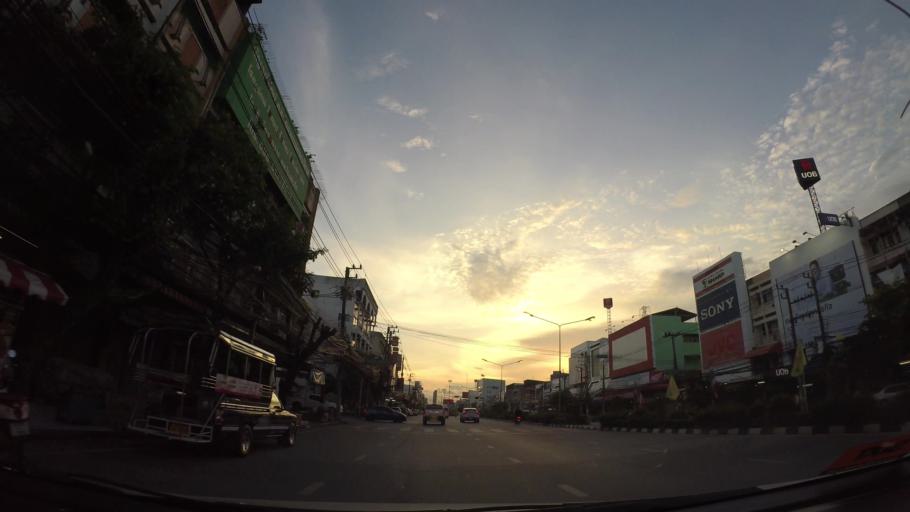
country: TH
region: Rayong
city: Rayong
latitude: 12.6819
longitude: 101.2727
